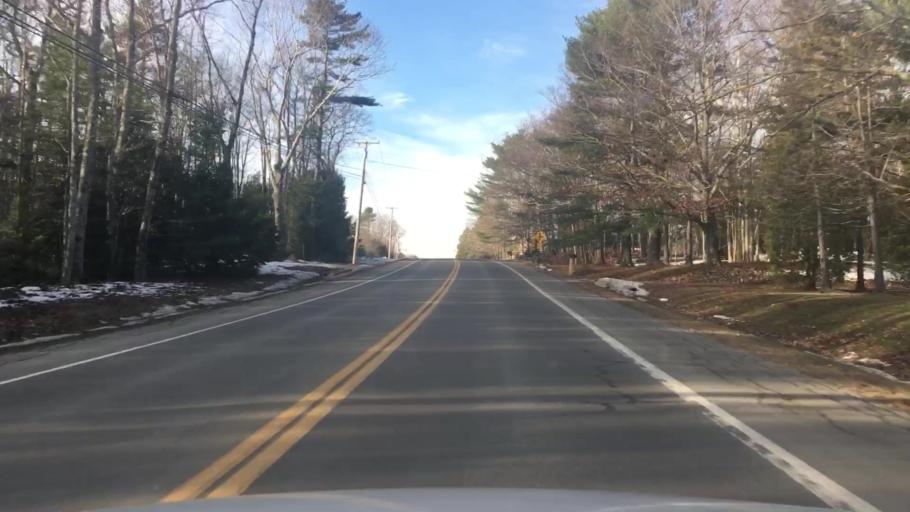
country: US
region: Maine
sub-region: Lincoln County
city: Wiscasset
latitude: 44.0468
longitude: -69.6785
